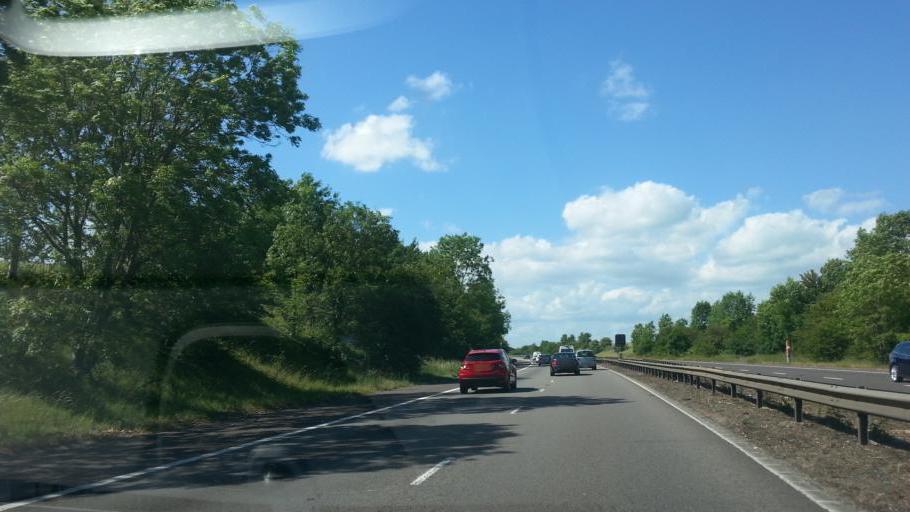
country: GB
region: England
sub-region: Hertfordshire
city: Baldock
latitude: 52.0014
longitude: -0.1976
